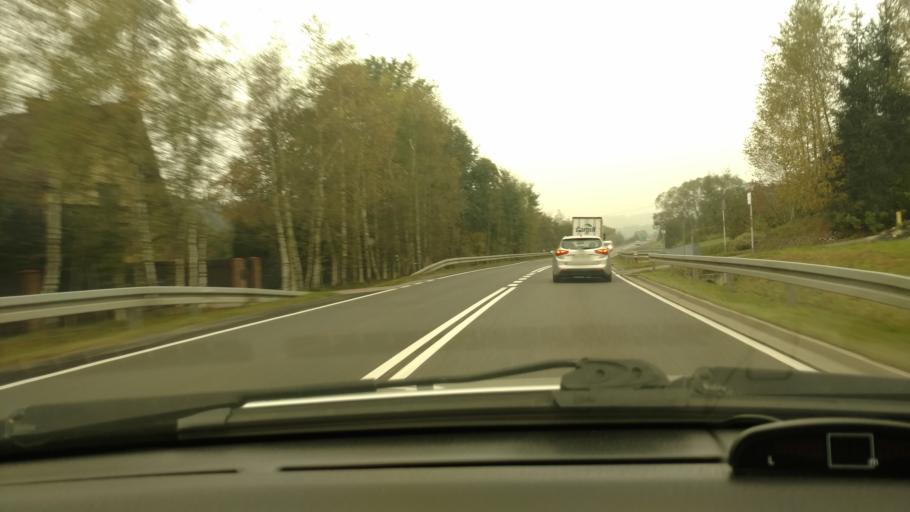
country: PL
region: Lesser Poland Voivodeship
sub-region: Powiat nowosadecki
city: Kamionka Wielka
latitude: 49.6155
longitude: 20.8097
